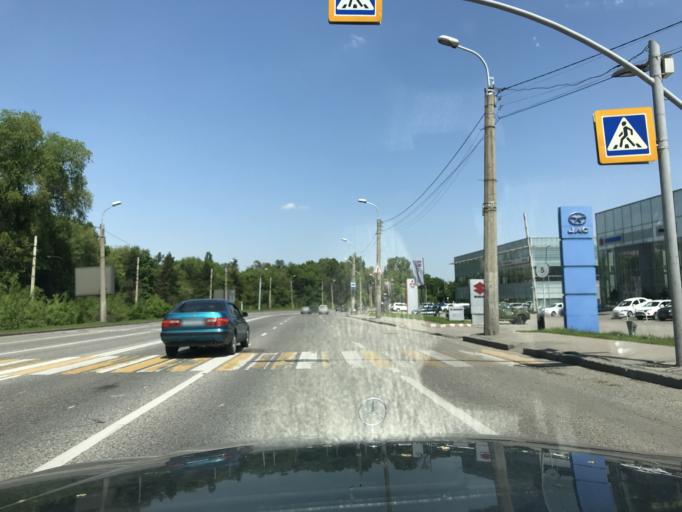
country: KZ
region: Almaty Qalasy
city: Almaty
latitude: 43.2958
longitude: 76.9486
